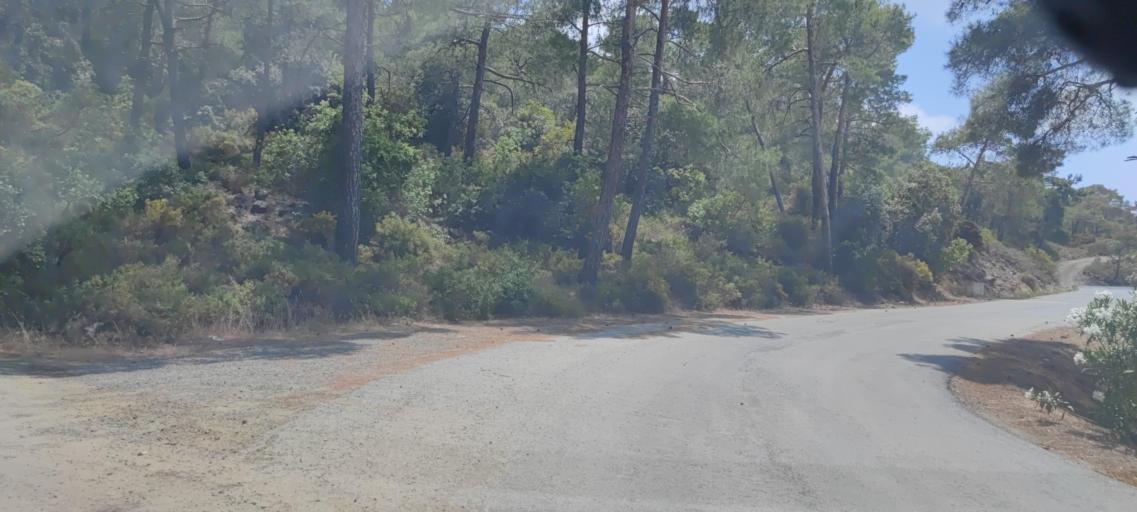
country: CY
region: Limassol
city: Pelendri
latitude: 34.8268
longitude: 33.0430
